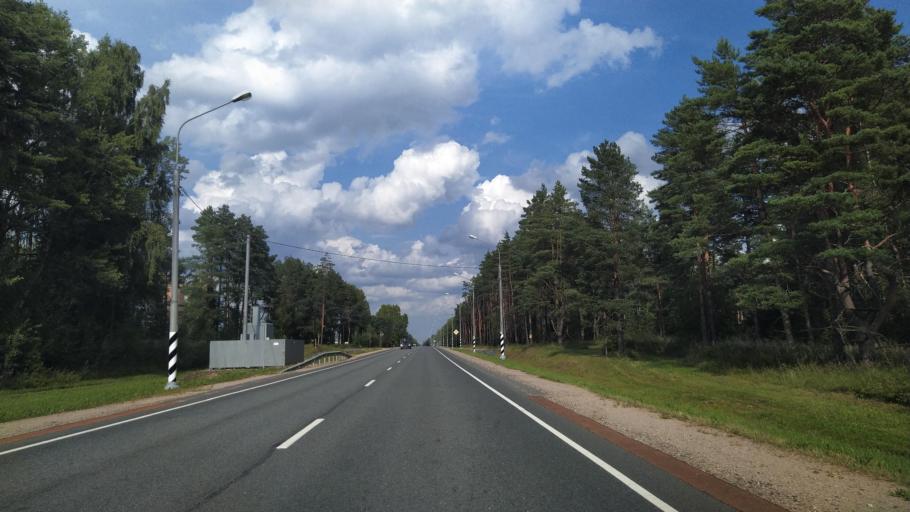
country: RU
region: Novgorod
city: Shimsk
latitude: 58.1785
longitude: 30.5329
